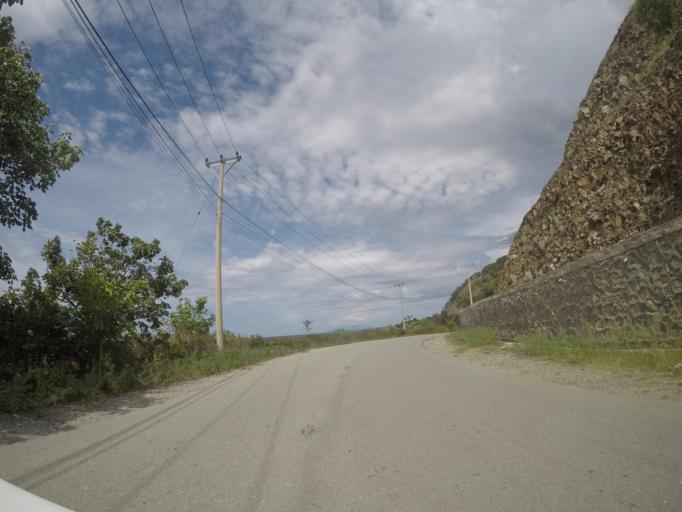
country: TL
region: Liquica
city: Maubara
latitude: -8.6260
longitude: 125.1618
